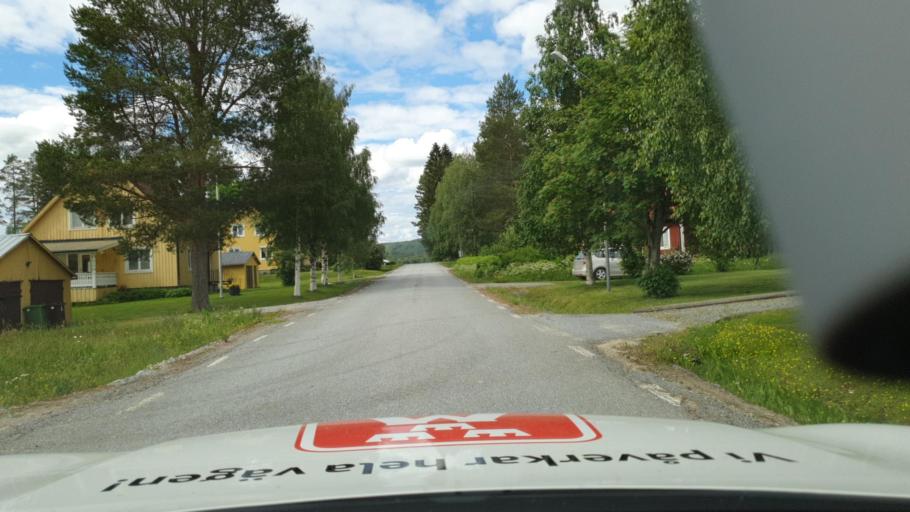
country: SE
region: Vaesterbotten
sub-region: Bjurholms Kommun
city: Bjurholm
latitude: 63.9176
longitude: 19.0703
